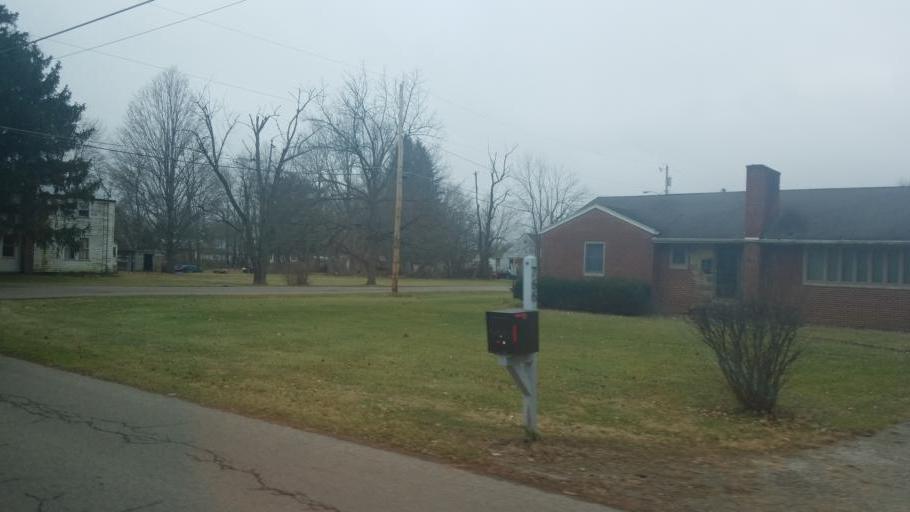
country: US
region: Ohio
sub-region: Crawford County
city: Galion
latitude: 40.7225
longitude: -82.7931
